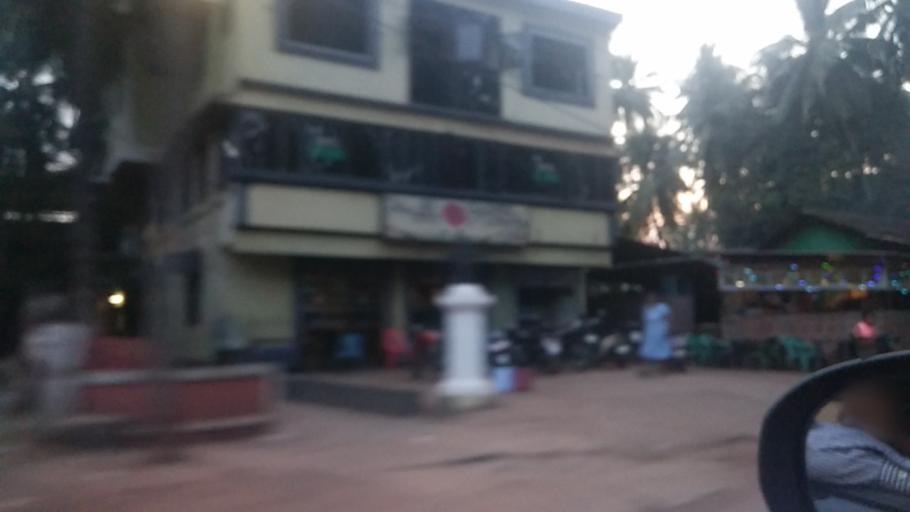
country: IN
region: Goa
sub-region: North Goa
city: Taleigao
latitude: 15.4700
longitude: 73.8252
